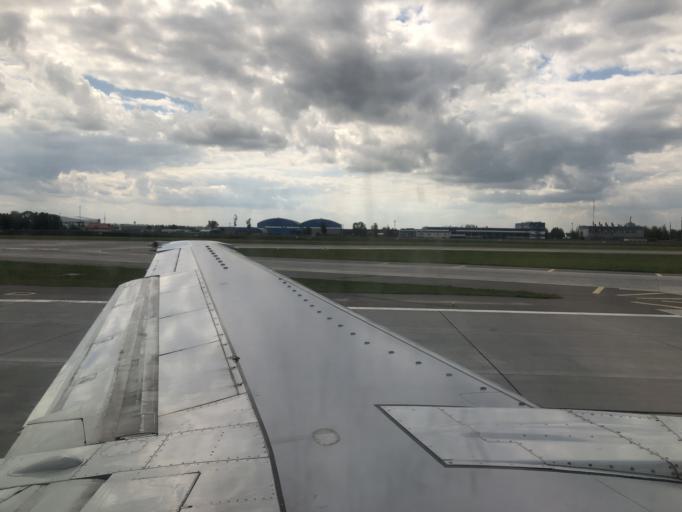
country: BY
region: Minsk
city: Horad Smalyavichy
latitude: 53.8873
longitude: 28.0594
